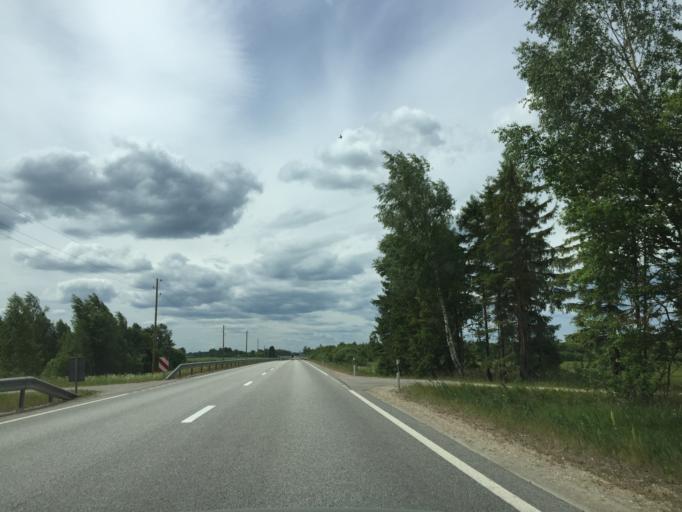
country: LV
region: Livani
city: Livani
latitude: 56.5344
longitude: 26.2897
